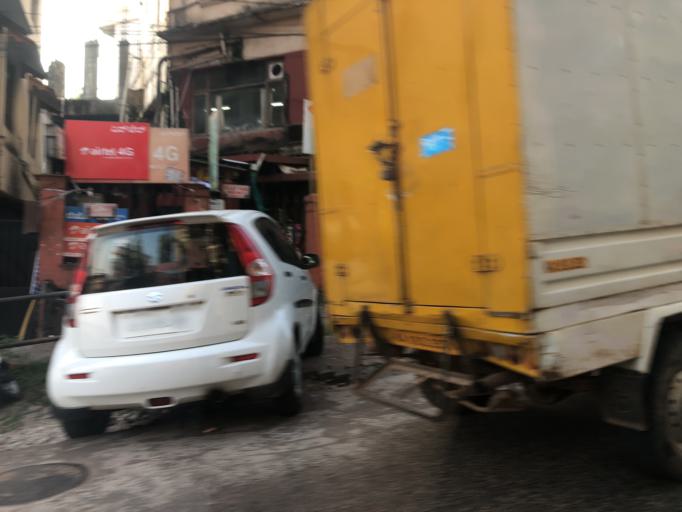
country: IN
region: Karnataka
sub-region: Dakshina Kannada
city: Mangalore
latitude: 12.8700
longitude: 74.8439
